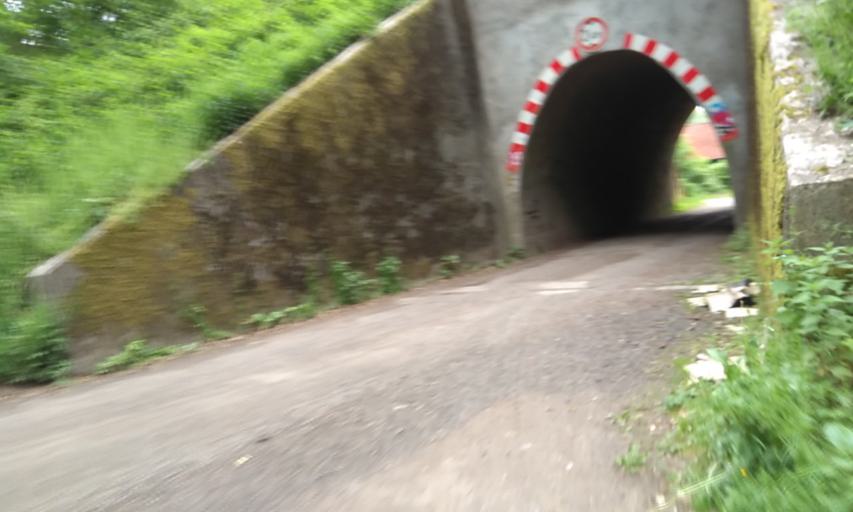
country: DE
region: Lower Saxony
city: Harsefeld
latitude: 53.4518
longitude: 9.4890
